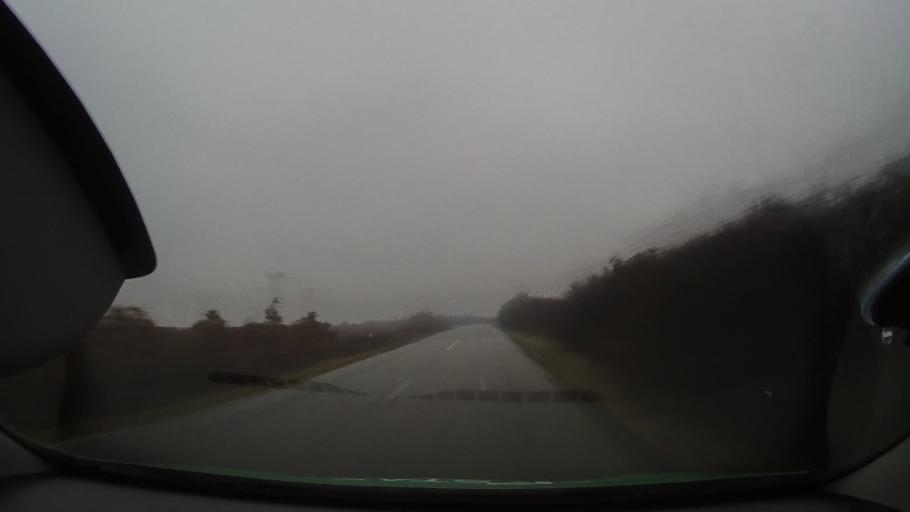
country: RO
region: Arad
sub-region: Comuna Craiova
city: Craiova
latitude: 46.6022
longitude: 21.9645
